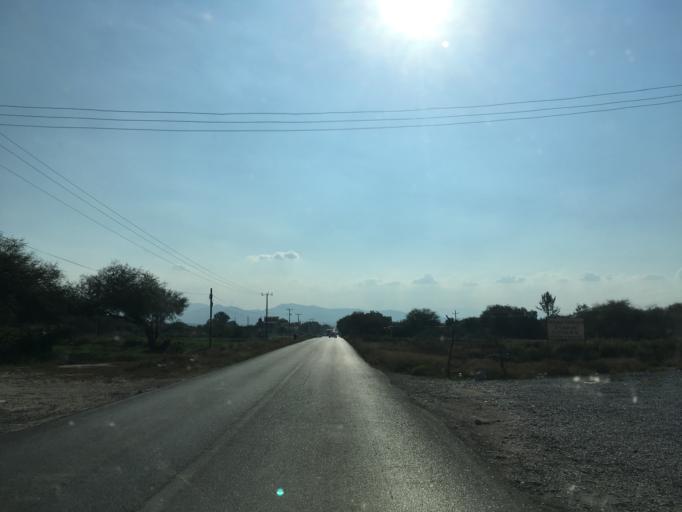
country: MX
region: Hidalgo
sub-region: Ixmiquilpan
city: El Nith
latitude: 20.5541
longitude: -99.1611
